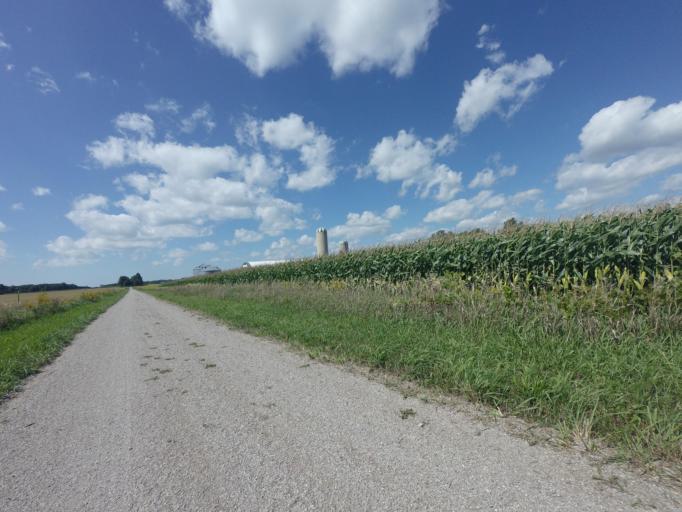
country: CA
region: Ontario
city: Huron East
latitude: 43.6645
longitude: -81.2614
